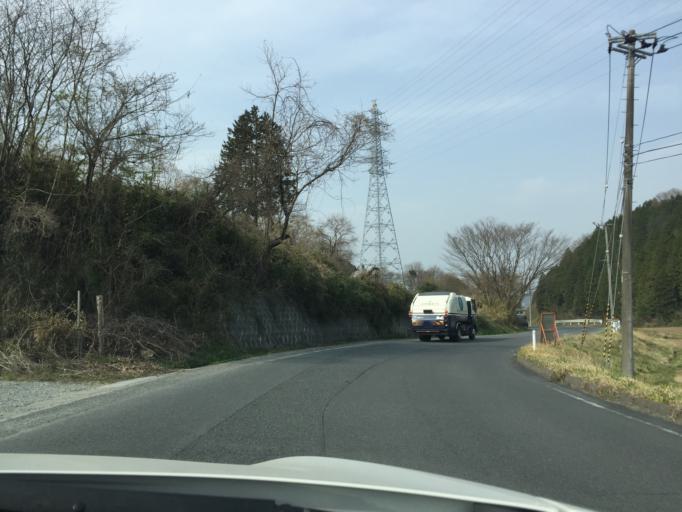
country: JP
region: Fukushima
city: Iwaki
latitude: 36.9738
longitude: 140.8545
